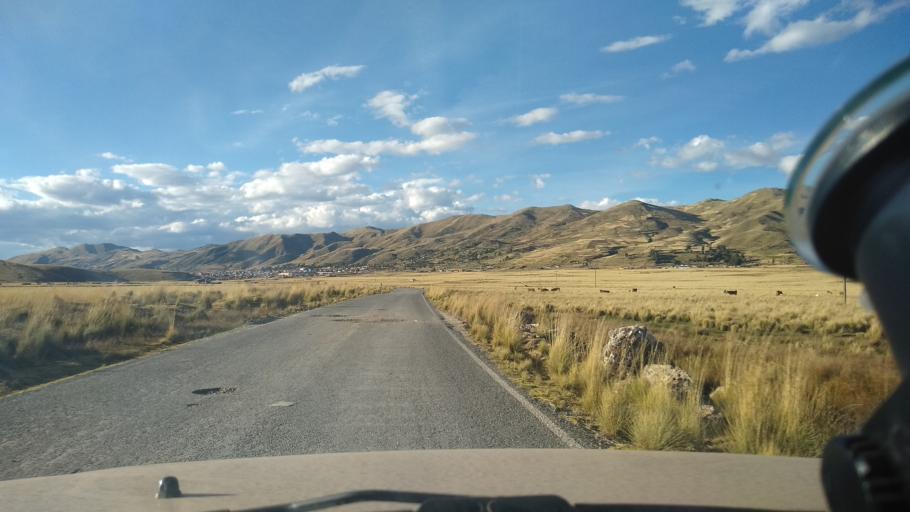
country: PE
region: Cusco
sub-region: Provincia de Canas
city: Chignayhua
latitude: -14.2436
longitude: -71.4336
